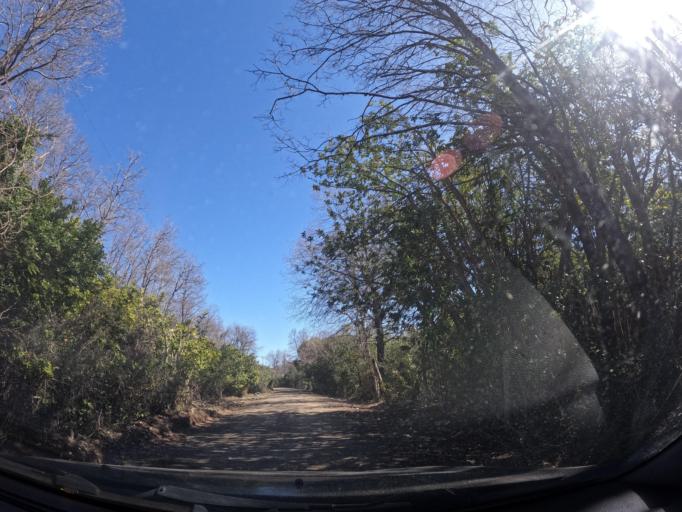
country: CL
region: Maule
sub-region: Provincia de Linares
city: Longavi
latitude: -36.2472
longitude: -71.3337
